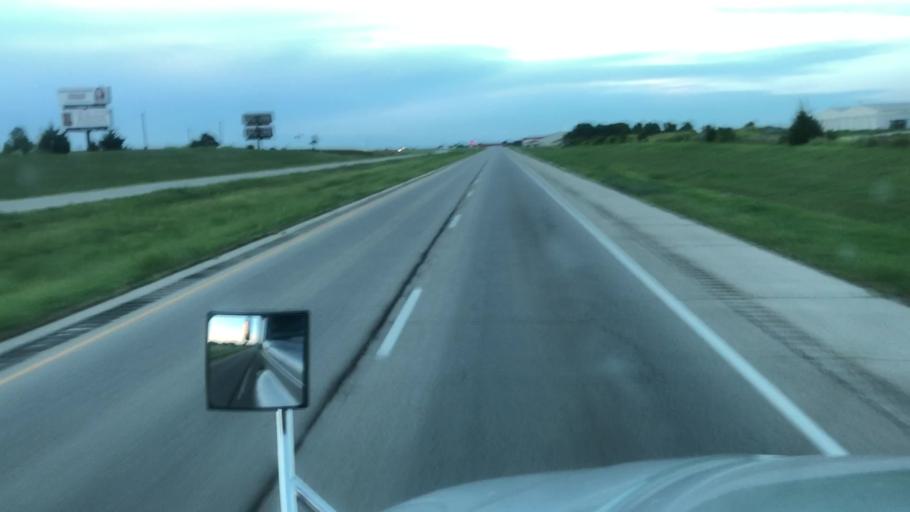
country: US
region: Oklahoma
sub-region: Kay County
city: Ponca City
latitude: 36.7583
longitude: -97.0644
